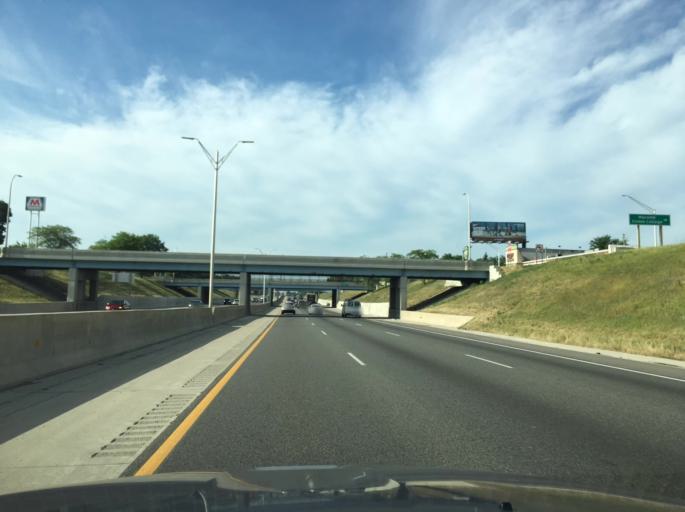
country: US
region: Michigan
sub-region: Macomb County
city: Roseville
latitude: 42.5116
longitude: -82.9185
